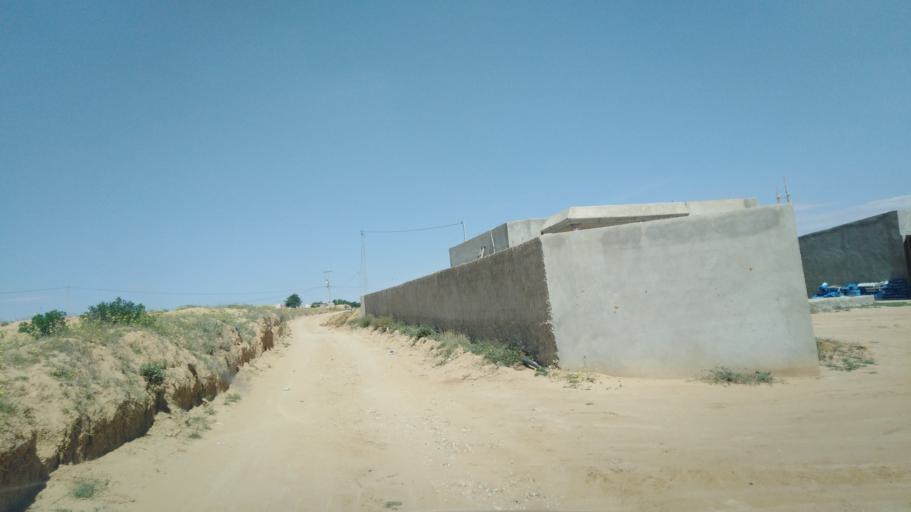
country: TN
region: Safaqis
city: Sfax
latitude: 34.7772
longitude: 10.5258
